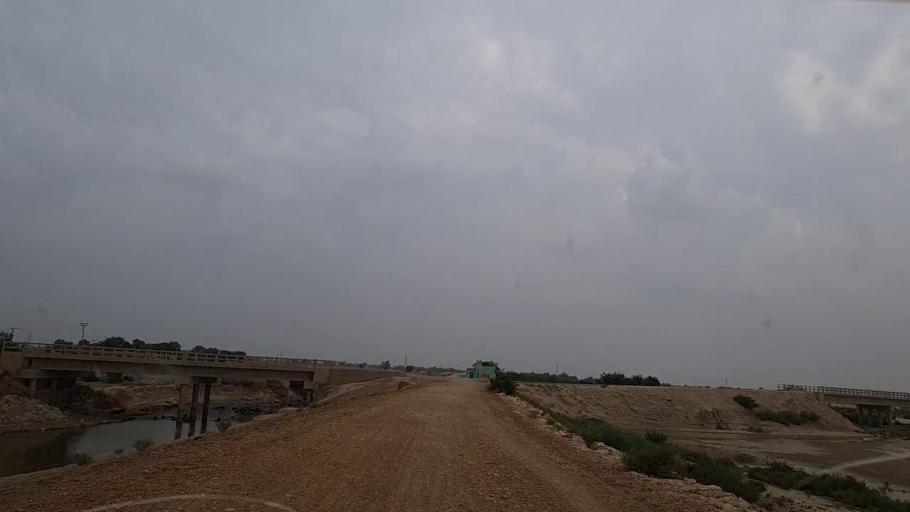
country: PK
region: Sindh
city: Johi
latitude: 26.6984
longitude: 67.5989
